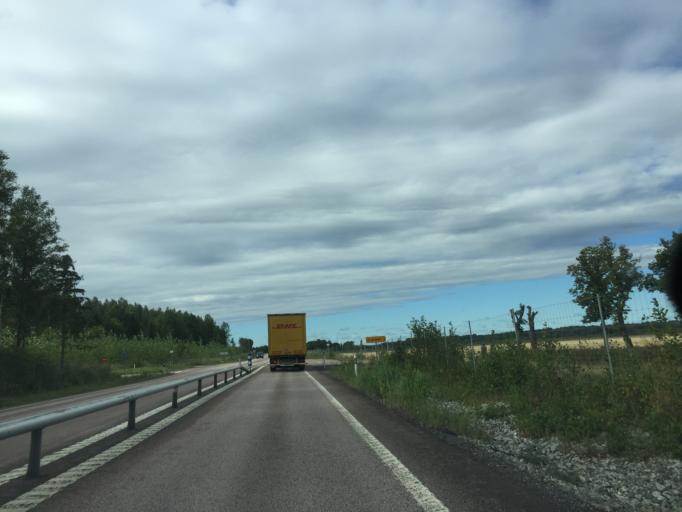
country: SE
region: Vaestmanland
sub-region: Kungsors Kommun
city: Kungsoer
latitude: 59.4100
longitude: 16.0118
